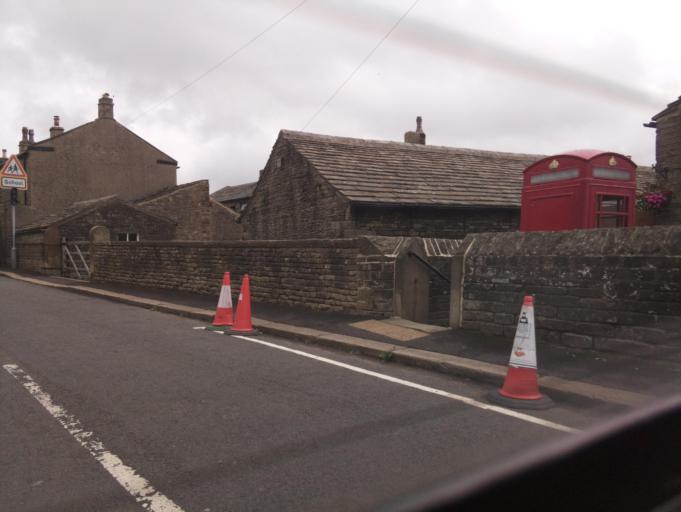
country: GB
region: England
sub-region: Kirklees
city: Meltham
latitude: 53.5493
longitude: -1.8387
